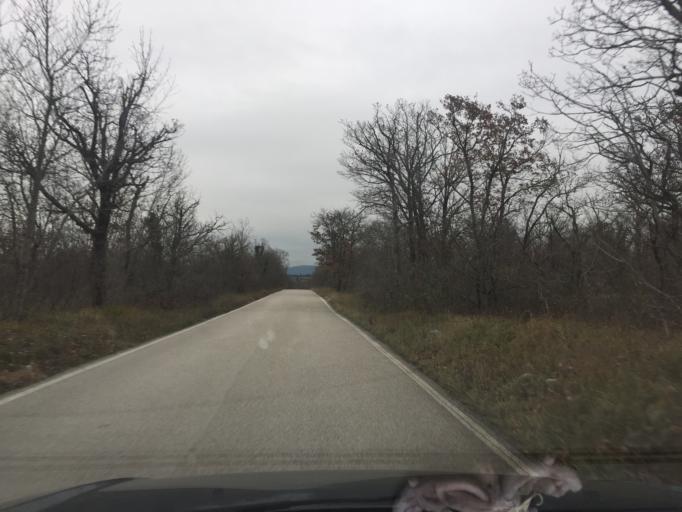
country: IT
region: Friuli Venezia Giulia
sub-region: Provincia di Trieste
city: Zolla
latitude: 45.7072
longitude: 13.8191
